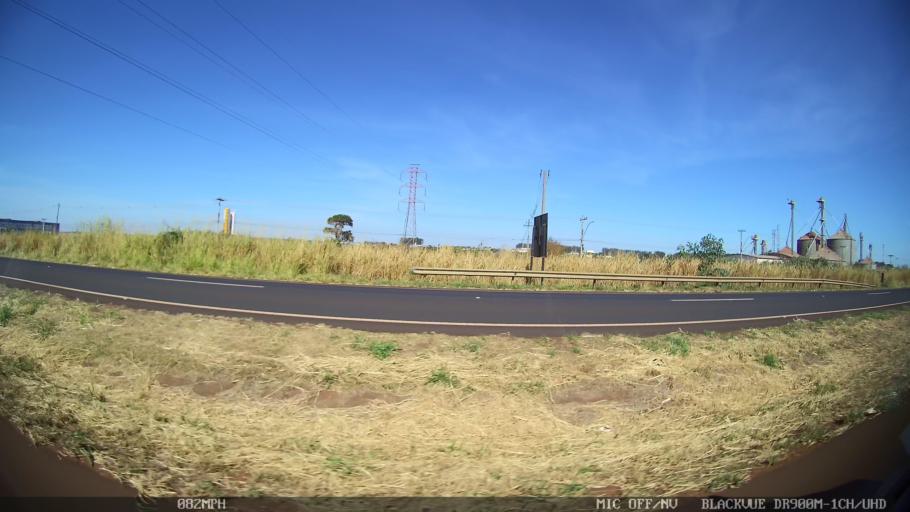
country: BR
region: Sao Paulo
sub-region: Barretos
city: Barretos
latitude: -20.5129
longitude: -48.5637
